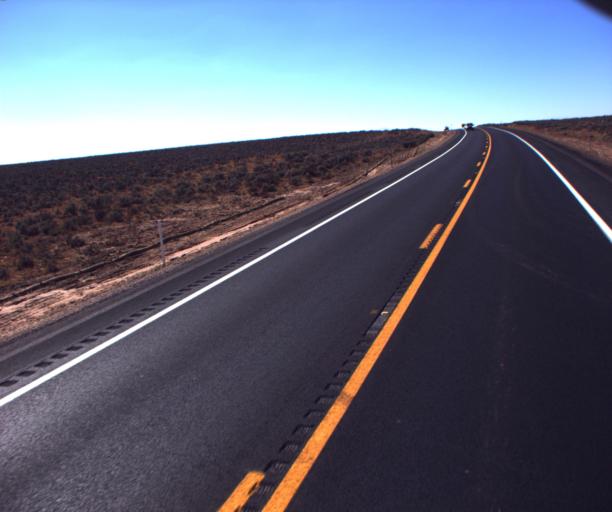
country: US
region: Arizona
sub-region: Apache County
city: Ganado
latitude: 35.7189
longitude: -109.4710
